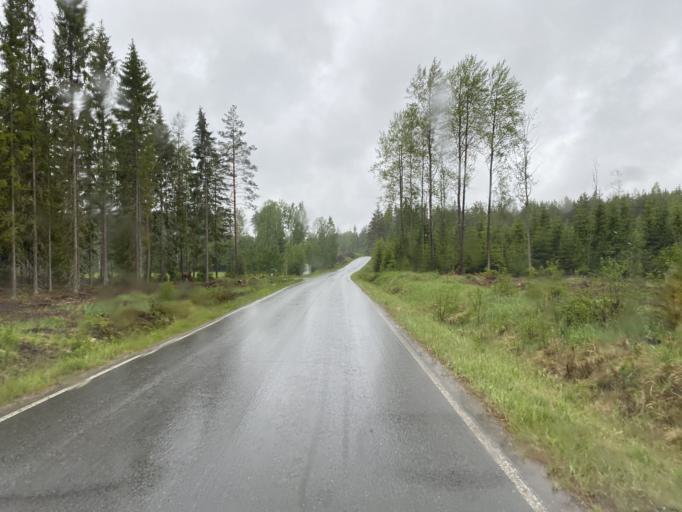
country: FI
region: Haeme
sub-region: Forssa
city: Humppila
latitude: 61.0832
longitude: 23.3111
